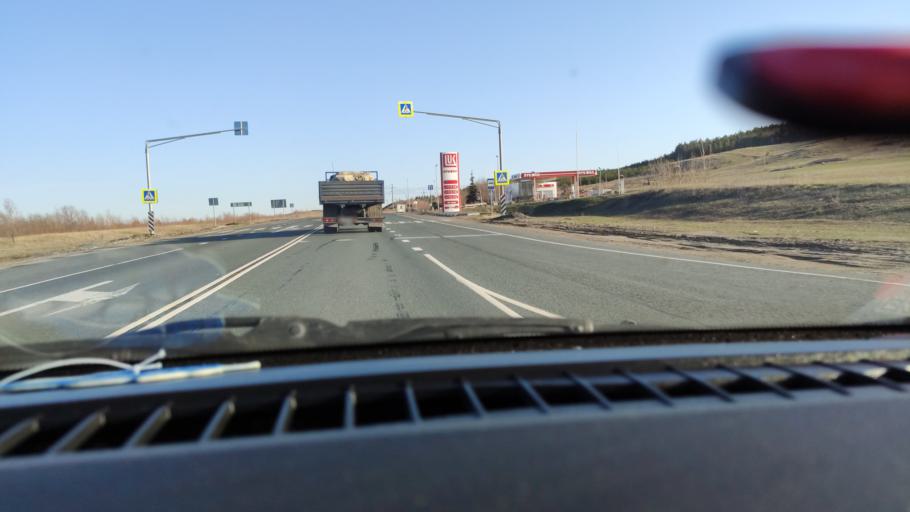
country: RU
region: Saratov
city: Alekseyevka
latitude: 52.2953
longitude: 47.9287
